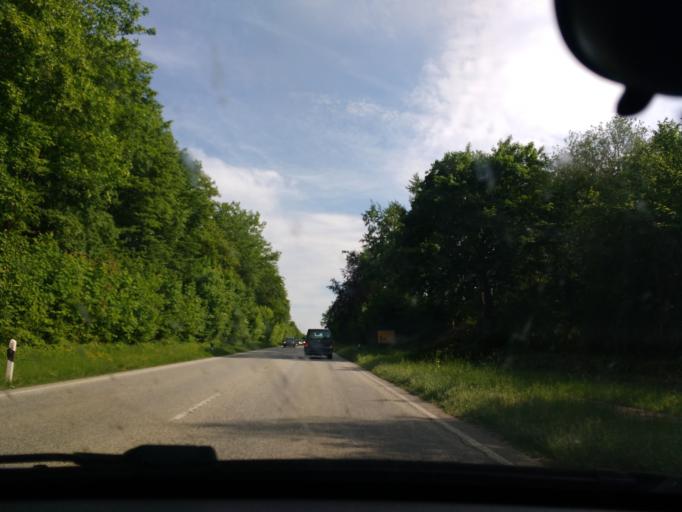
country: DE
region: Schleswig-Holstein
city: Pogeez
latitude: 53.7362
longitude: 10.7347
